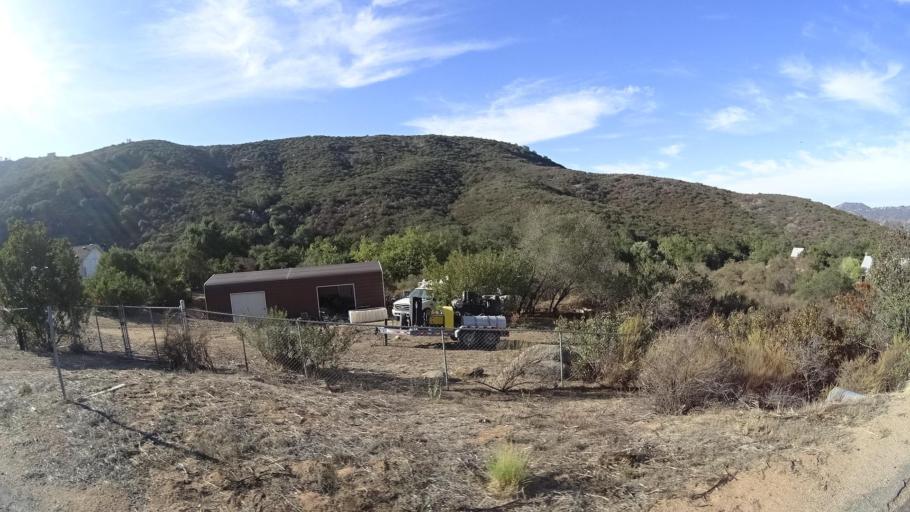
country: US
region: California
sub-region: San Diego County
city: Harbison Canyon
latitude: 32.8069
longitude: -116.7987
